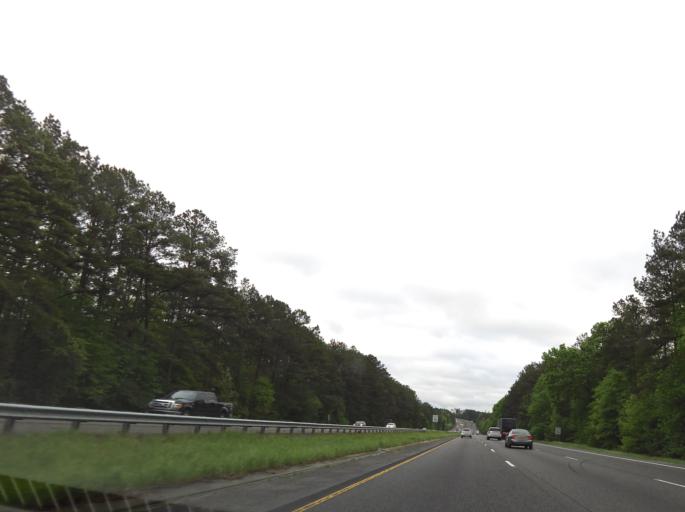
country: US
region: Georgia
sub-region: Butts County
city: Indian Springs
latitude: 33.1566
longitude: -84.0355
